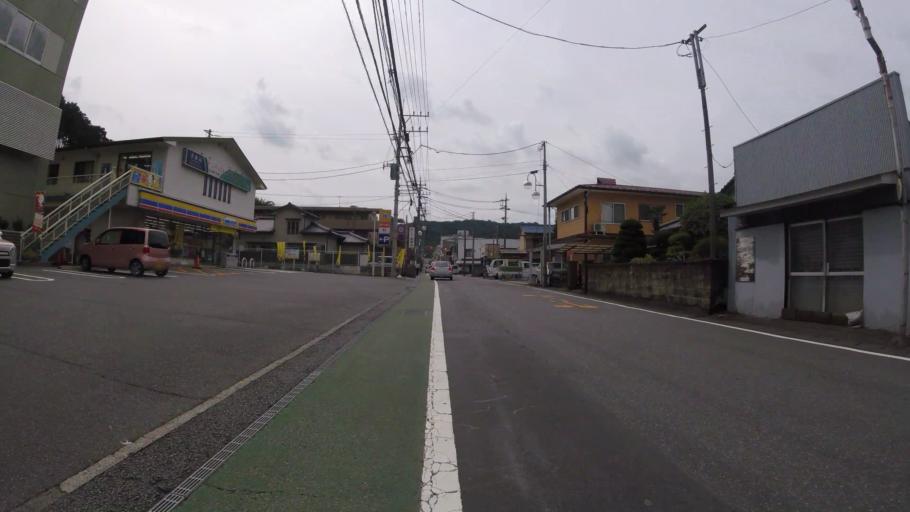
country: JP
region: Shizuoka
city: Mishima
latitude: 34.9966
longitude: 138.9389
